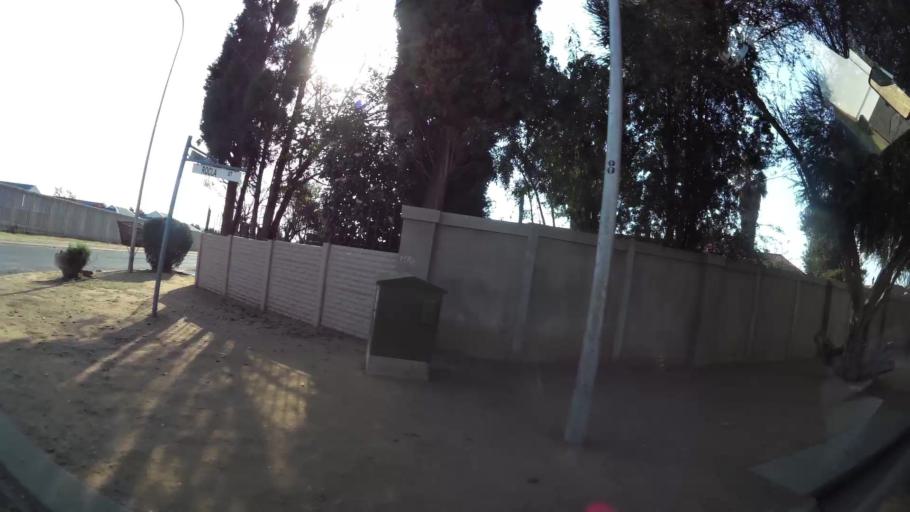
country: ZA
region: Gauteng
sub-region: Ekurhuleni Metropolitan Municipality
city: Benoni
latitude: -26.1269
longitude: 28.3663
